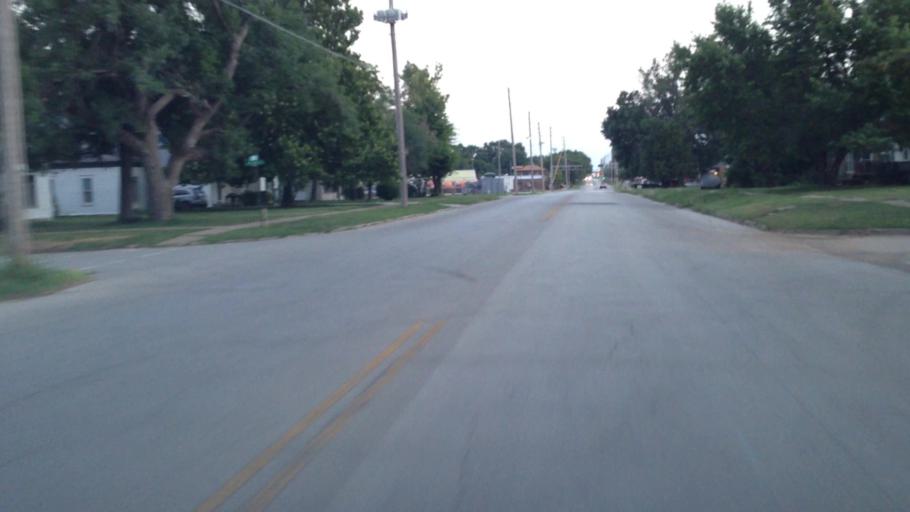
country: US
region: Kansas
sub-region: Montgomery County
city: Independence
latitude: 37.2347
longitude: -95.7107
